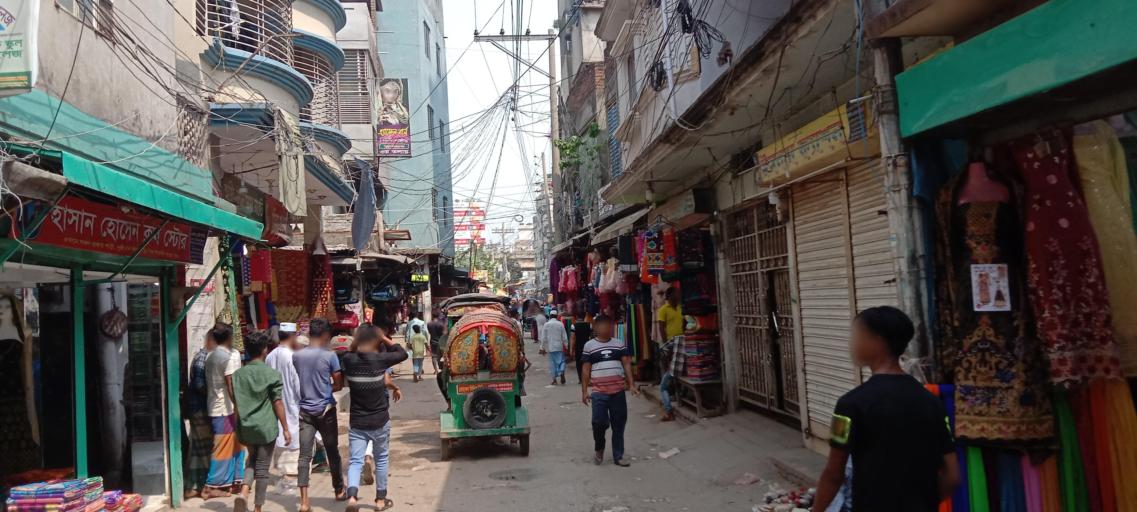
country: BD
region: Dhaka
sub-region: Dhaka
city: Dhaka
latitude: 23.7074
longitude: 90.3988
